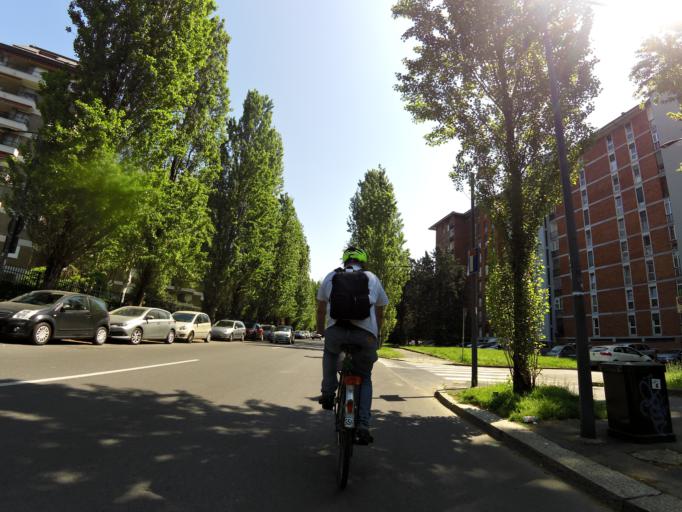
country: IT
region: Lombardy
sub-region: Citta metropolitana di Milano
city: Sesto San Giovanni
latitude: 45.4913
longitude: 9.2431
